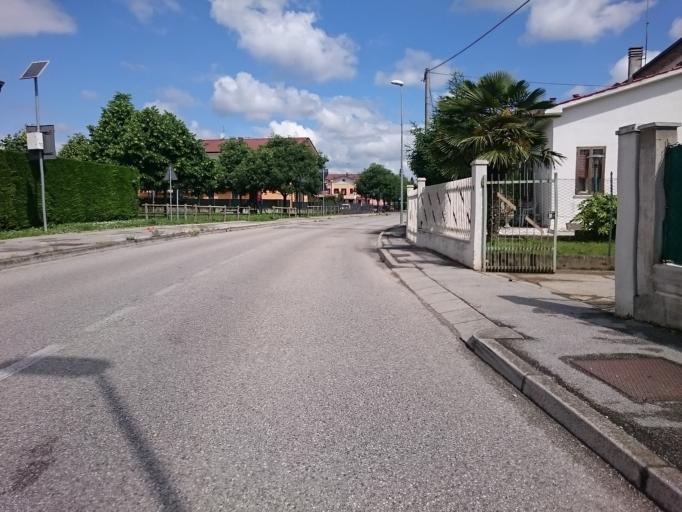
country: IT
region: Veneto
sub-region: Provincia di Padova
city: Mestrino
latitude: 45.4578
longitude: 11.7485
